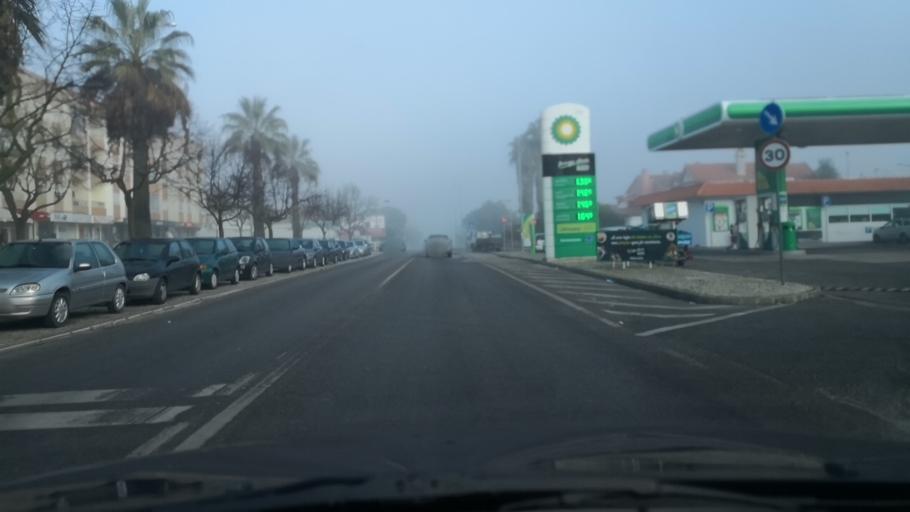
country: PT
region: Setubal
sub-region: Palmela
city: Pinhal Novo
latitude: 38.6362
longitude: -8.9146
